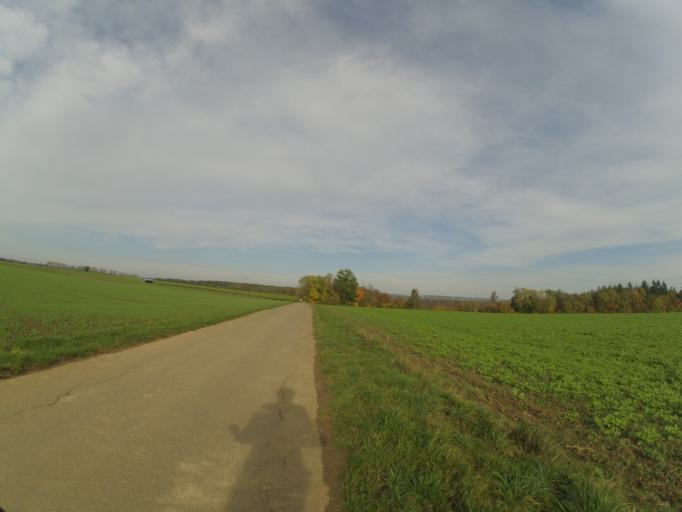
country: DE
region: Baden-Wuerttemberg
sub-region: Tuebingen Region
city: Blaubeuren
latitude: 48.4382
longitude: 9.8635
